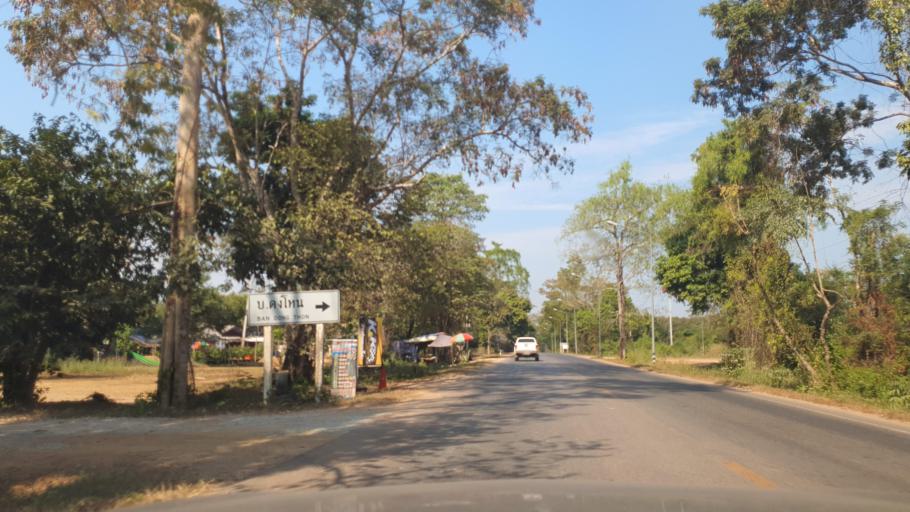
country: TH
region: Nakhon Phanom
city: Ban Phaeng
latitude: 18.0155
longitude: 104.1555
